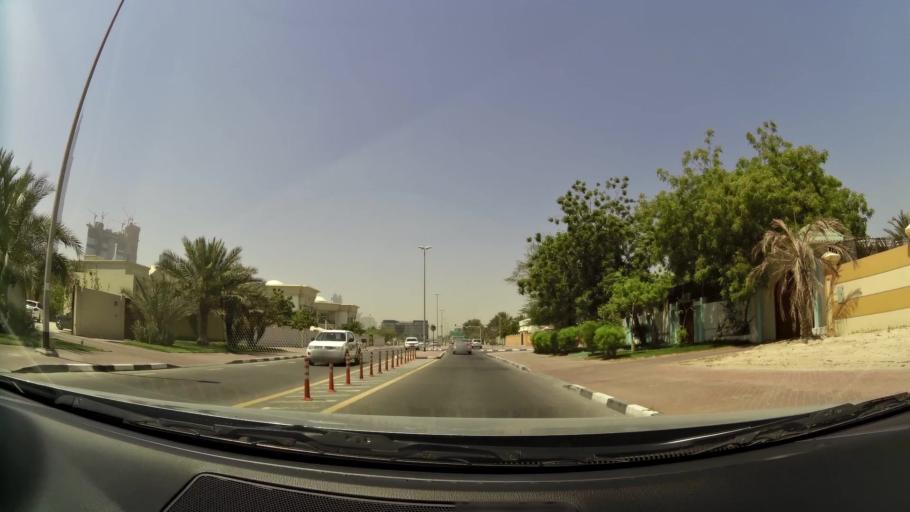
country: AE
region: Dubai
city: Dubai
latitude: 25.2120
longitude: 55.2683
